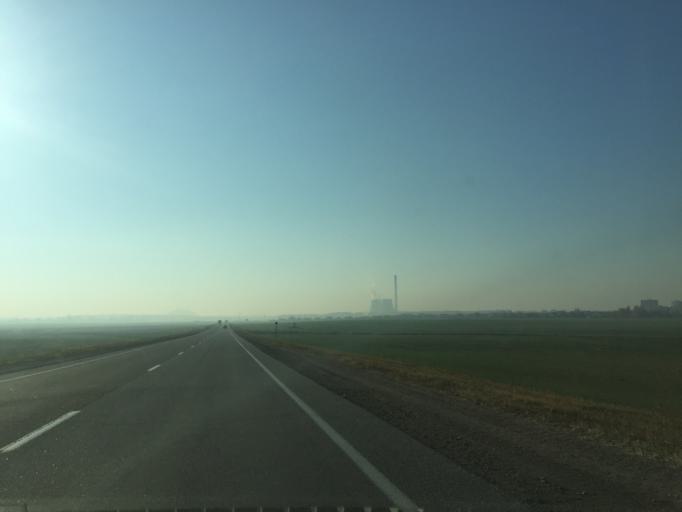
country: BY
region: Gomel
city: Kastsyukowka
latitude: 52.4744
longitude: 30.8223
